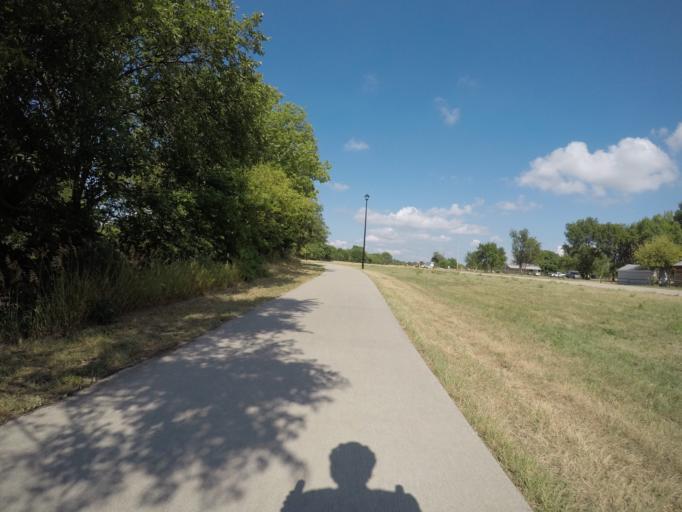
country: US
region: Nebraska
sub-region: Buffalo County
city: Kearney
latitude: 40.6742
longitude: -99.0640
